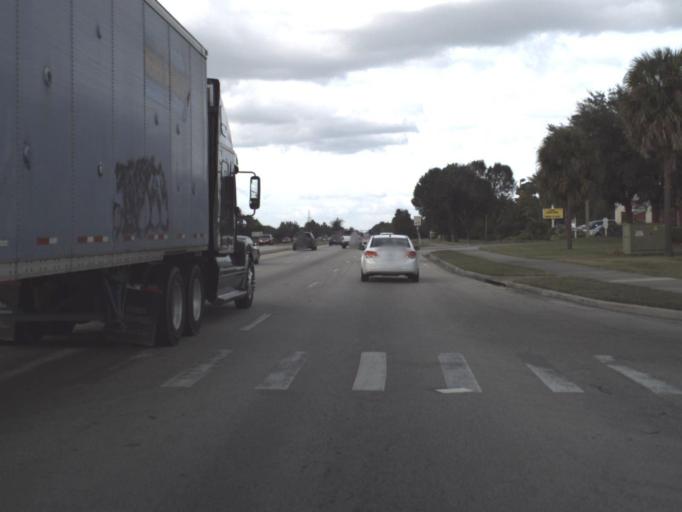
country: US
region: Florida
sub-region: Orange County
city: Oak Ridge
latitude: 28.4870
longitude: -81.4173
